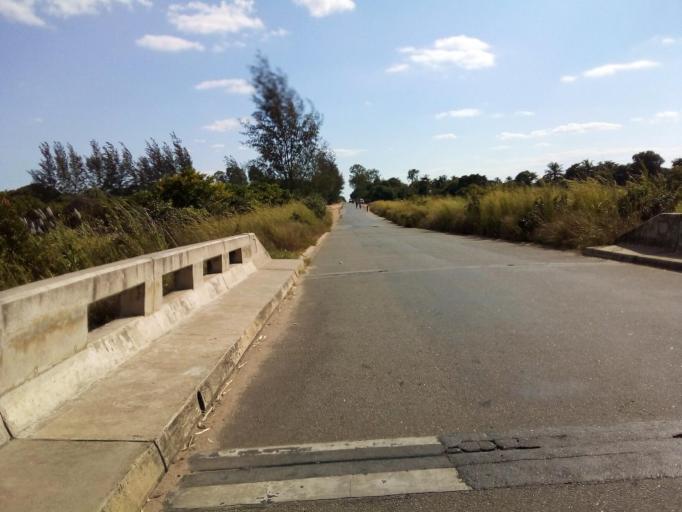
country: MZ
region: Zambezia
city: Quelimane
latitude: -17.5764
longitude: 36.6463
